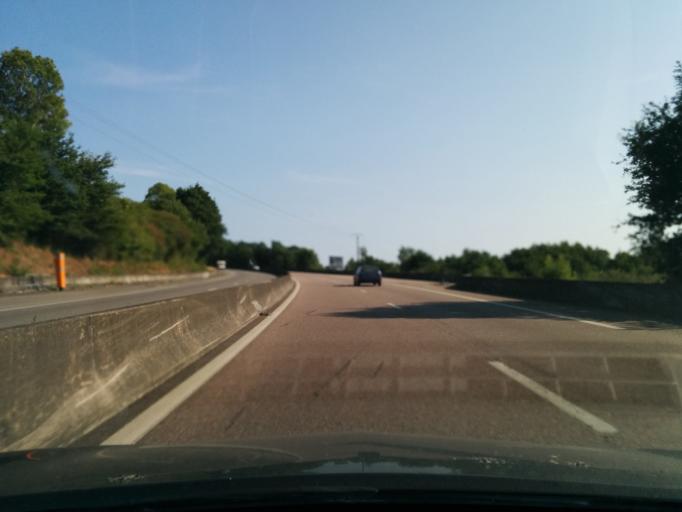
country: FR
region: Limousin
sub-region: Departement de la Haute-Vienne
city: Boisseuil
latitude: 45.7311
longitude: 1.3403
